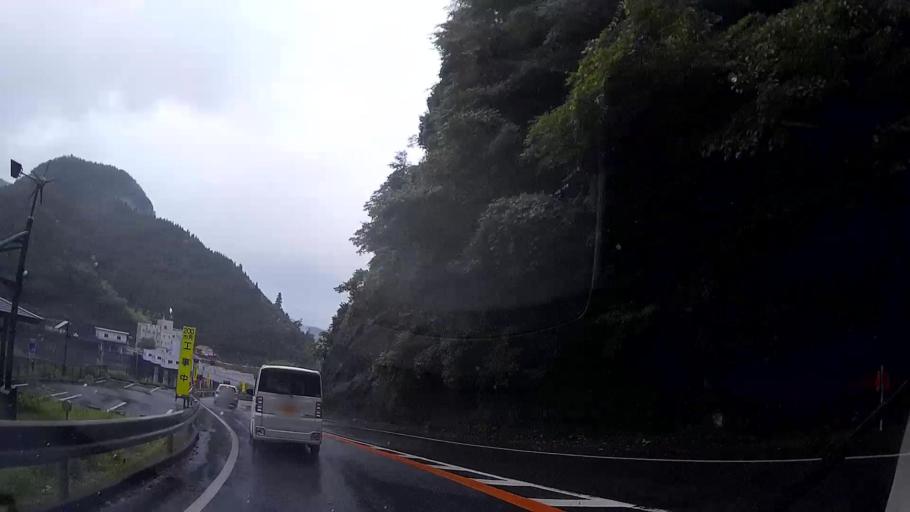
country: JP
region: Oita
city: Hita
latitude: 33.1928
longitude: 130.9949
